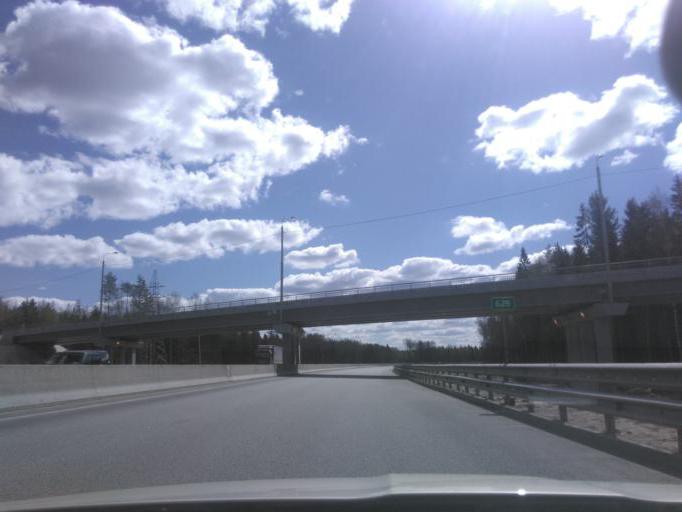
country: RU
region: Moskovskaya
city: Peshki
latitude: 56.1391
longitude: 37.0933
